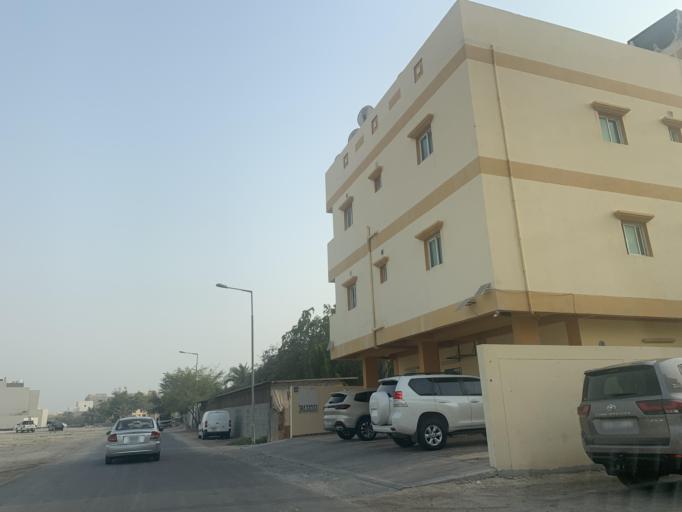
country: BH
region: Manama
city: Jidd Hafs
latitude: 26.2226
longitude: 50.5189
